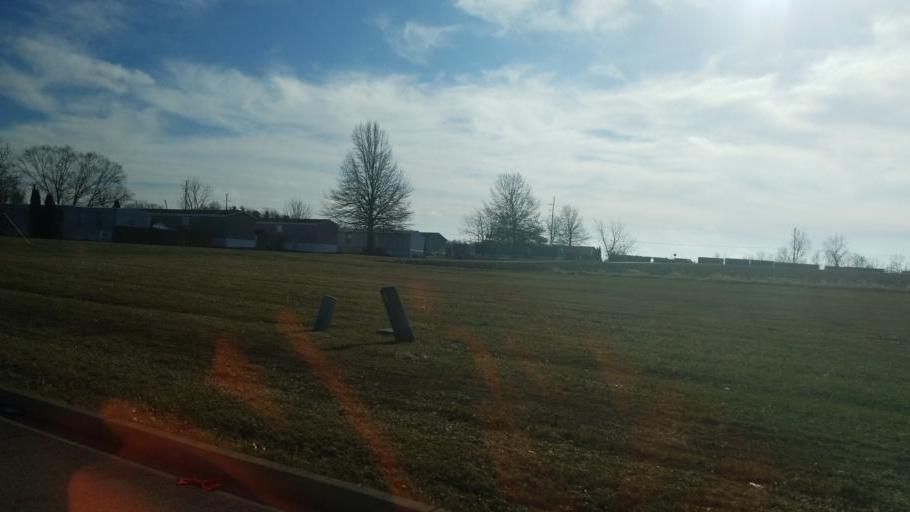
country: US
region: Ohio
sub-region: Crawford County
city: Crestline
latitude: 40.7717
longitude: -82.7497
